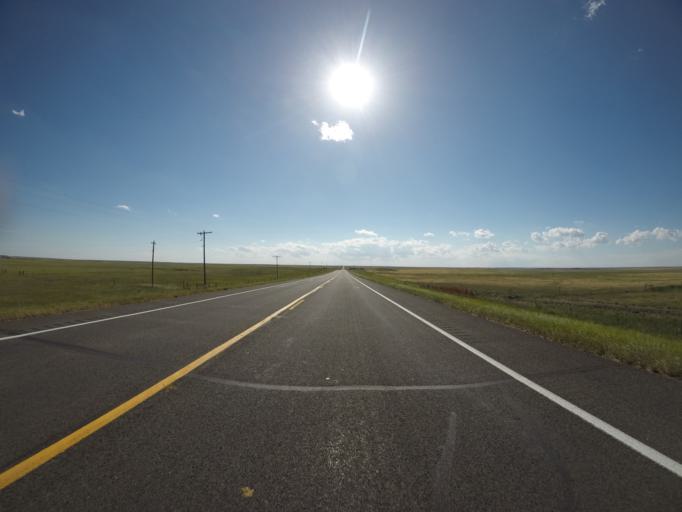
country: US
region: Colorado
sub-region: Morgan County
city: Brush
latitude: 40.6106
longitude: -103.6095
